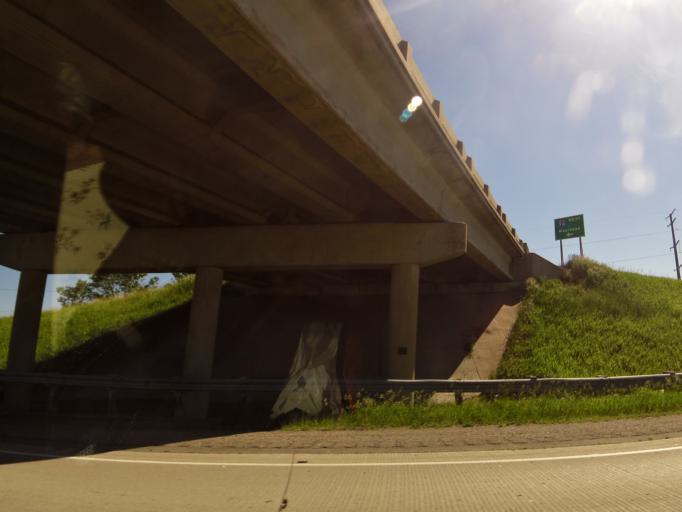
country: US
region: Minnesota
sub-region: Clay County
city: Barnesville
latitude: 46.5583
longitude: -96.3159
